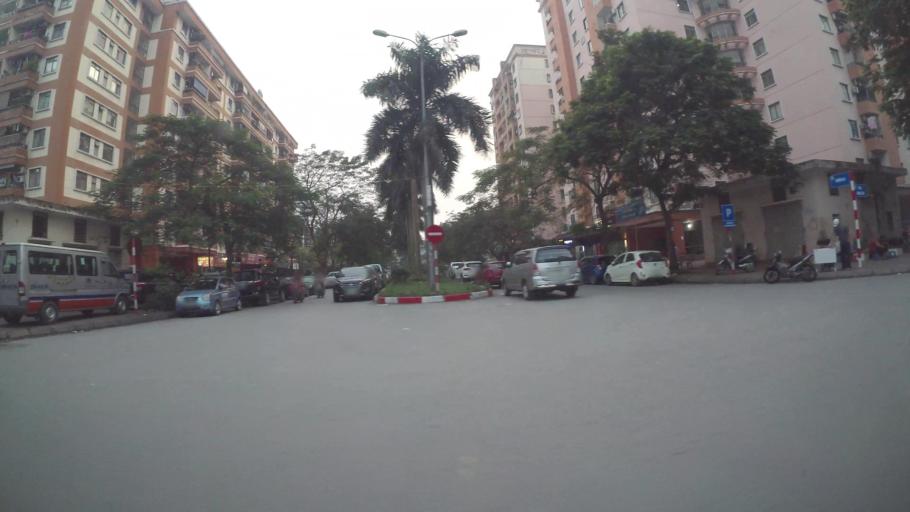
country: VN
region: Ha Noi
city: Ha Dong
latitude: 20.9740
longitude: 105.7888
